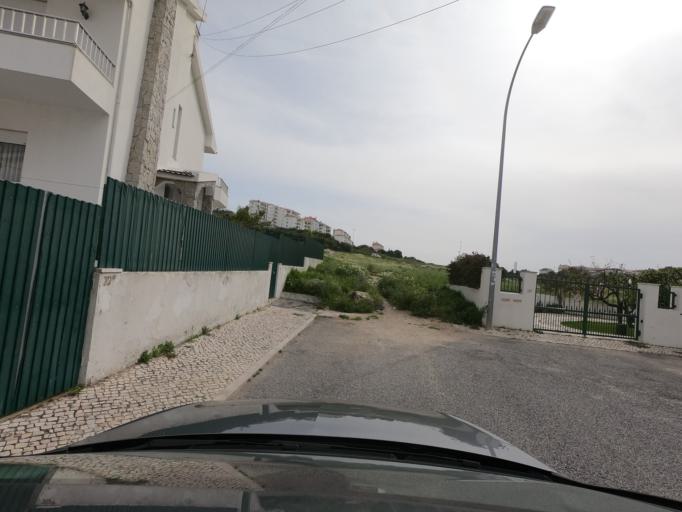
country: PT
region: Lisbon
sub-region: Oeiras
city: Porto Salvo
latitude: 38.7169
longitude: -9.2979
